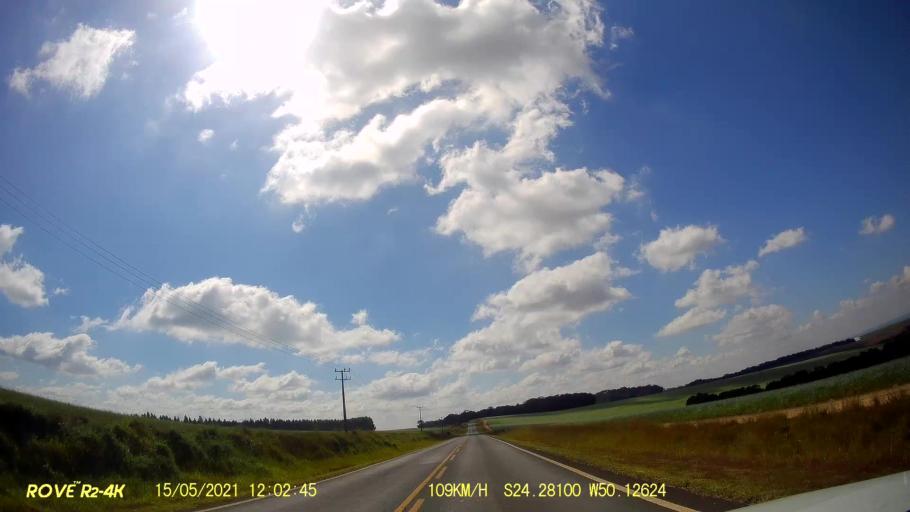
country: BR
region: Parana
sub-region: Pirai Do Sul
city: Pirai do Sul
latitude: -24.2813
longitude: -50.1265
